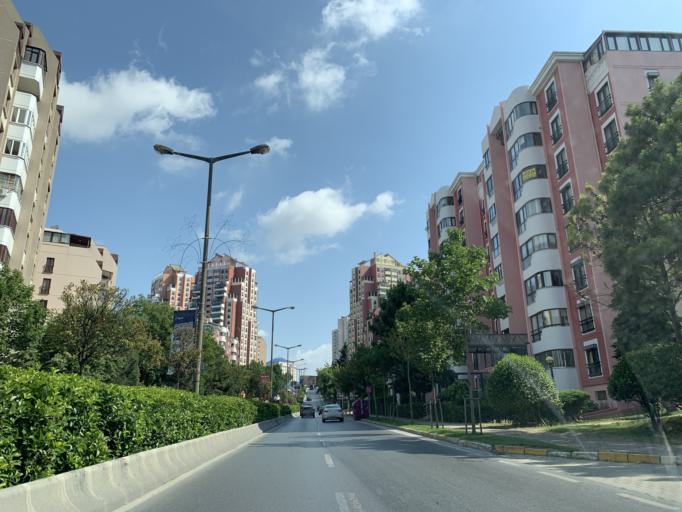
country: TR
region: Istanbul
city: Esenyurt
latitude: 41.0672
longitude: 28.6844
